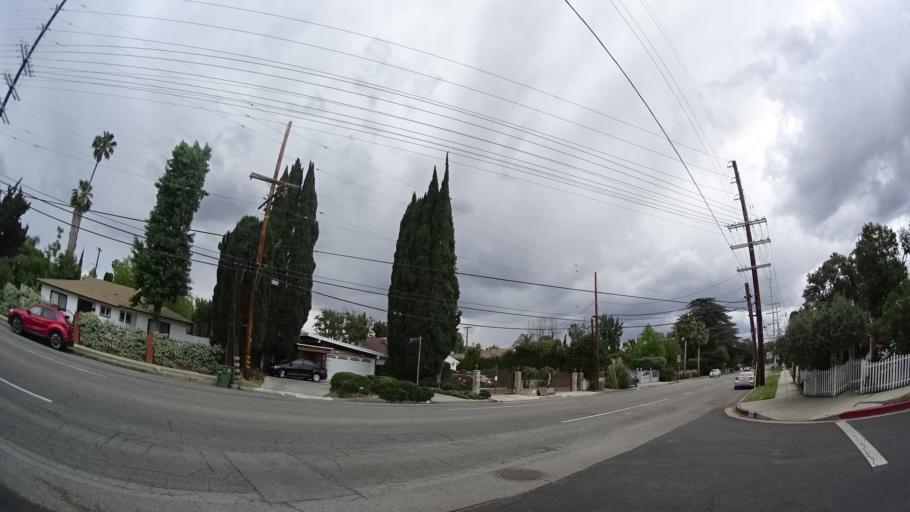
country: US
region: California
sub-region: Los Angeles County
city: Sherman Oaks
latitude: 34.1648
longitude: -118.4260
